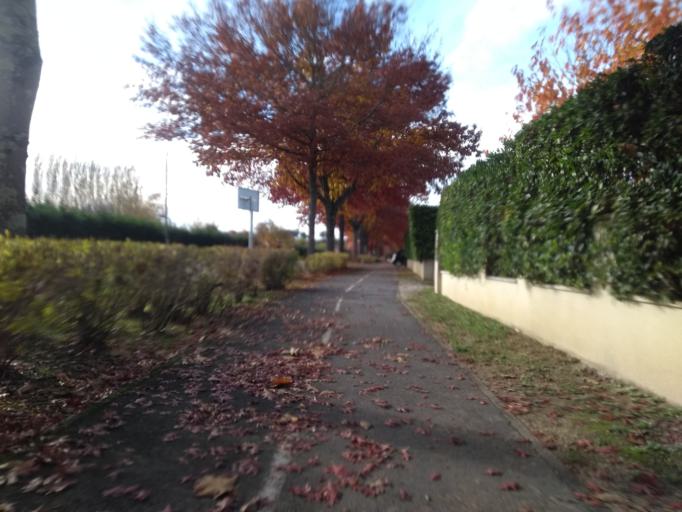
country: FR
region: Aquitaine
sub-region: Departement de la Gironde
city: Canejan
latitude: 44.7626
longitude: -0.6477
